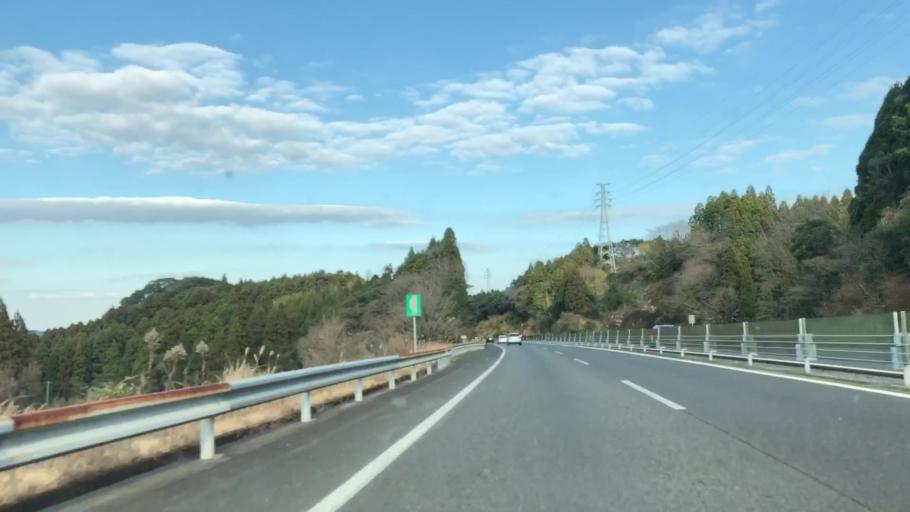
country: JP
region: Miyazaki
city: Miyazaki-shi
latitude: 31.8352
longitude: 131.3428
